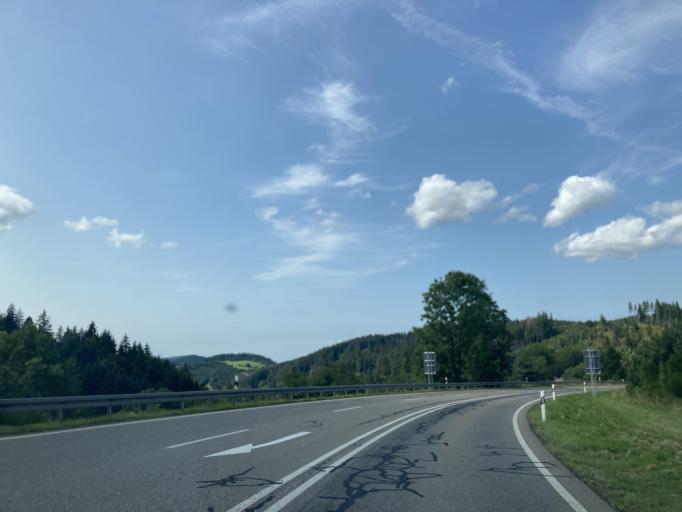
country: DE
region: Baden-Wuerttemberg
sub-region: Freiburg Region
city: Sankt Georgen im Schwarzwald
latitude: 48.1266
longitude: 8.2899
